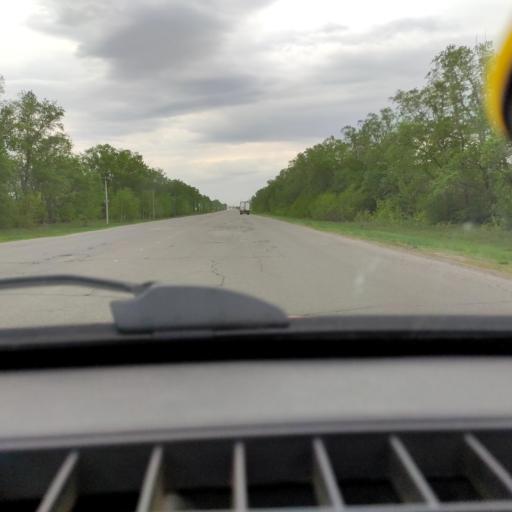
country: RU
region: Samara
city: Tol'yatti
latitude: 53.5947
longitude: 49.4074
